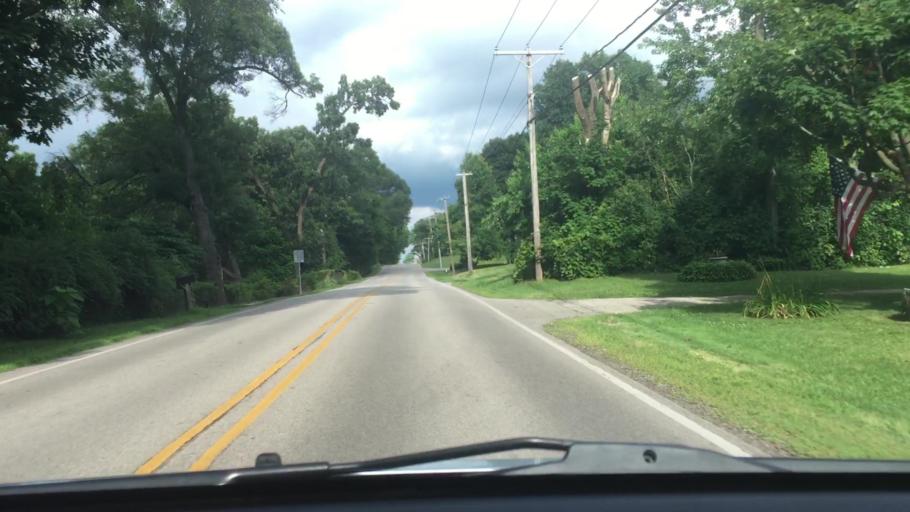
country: US
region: Illinois
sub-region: McHenry County
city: Crystal Lake
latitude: 42.2626
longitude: -88.3288
